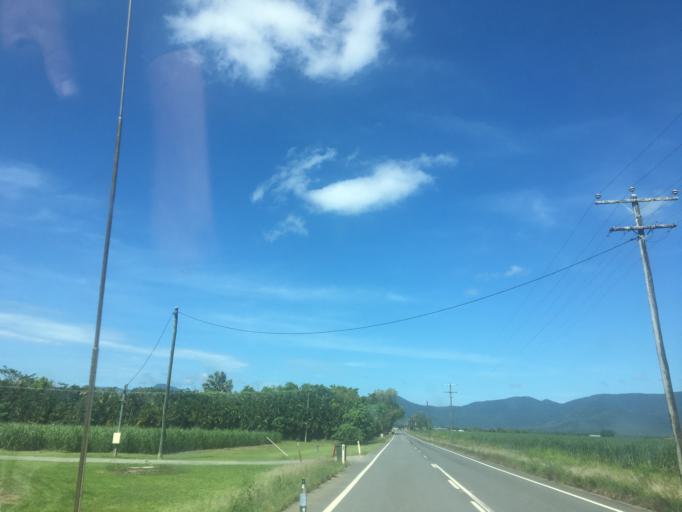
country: AU
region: Queensland
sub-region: Cairns
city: Woree
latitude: -17.0635
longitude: 145.7571
